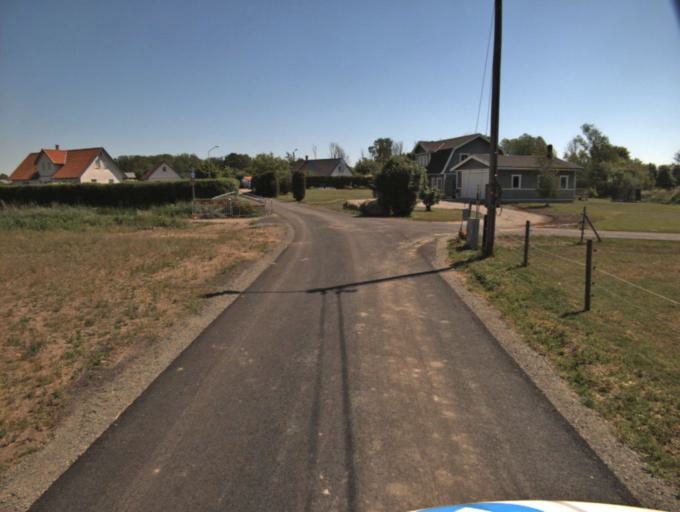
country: SE
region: Skane
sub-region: Kristianstads Kommun
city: Kristianstad
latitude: 56.0141
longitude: 14.2168
